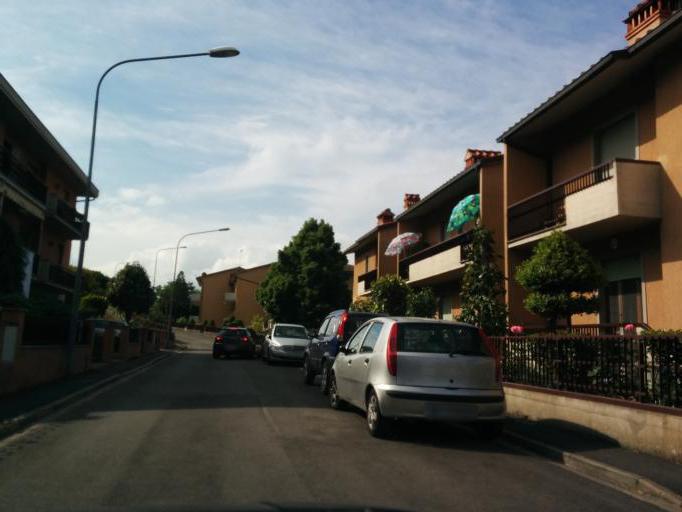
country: IT
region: Tuscany
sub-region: Province of Florence
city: Mercatale
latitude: 43.6160
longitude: 11.1907
